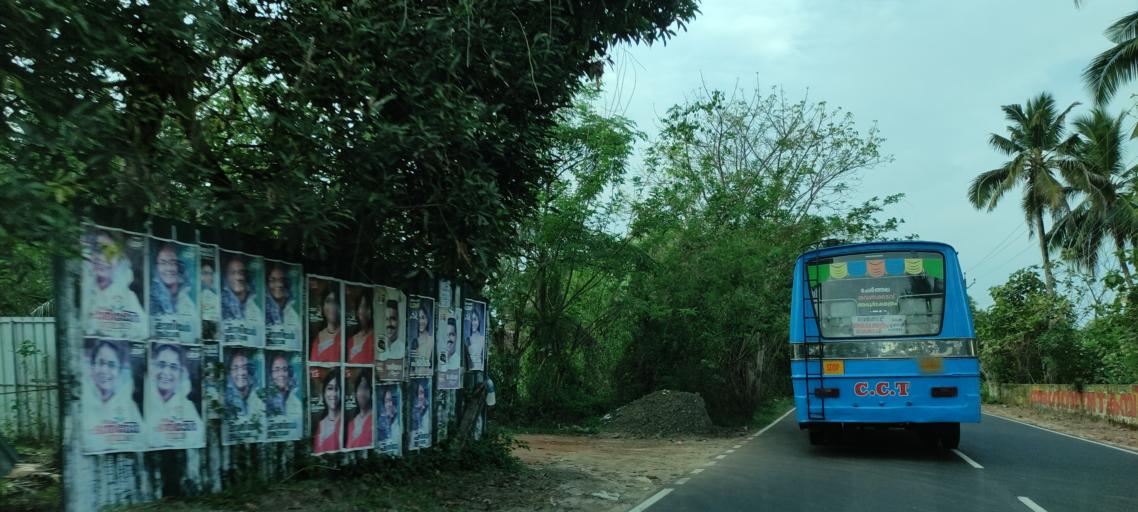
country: IN
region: Kerala
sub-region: Alappuzha
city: Kutiatodu
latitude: 9.7853
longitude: 76.3597
